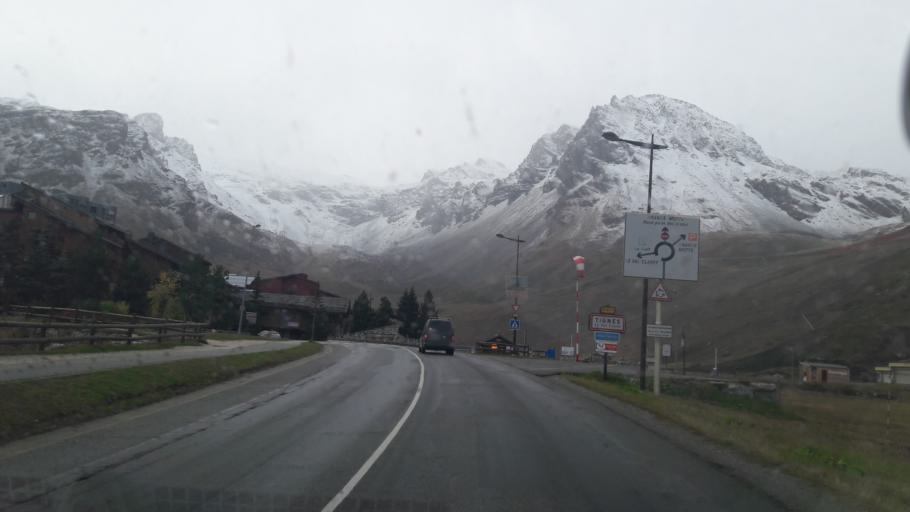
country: FR
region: Rhone-Alpes
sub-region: Departement de la Savoie
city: Tignes
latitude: 45.4591
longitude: 6.8993
